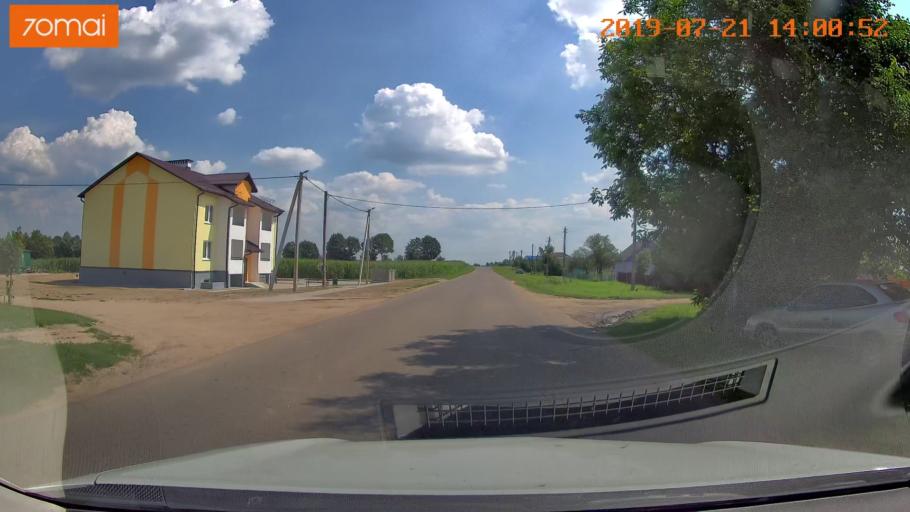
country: BY
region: Grodnenskaya
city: Lyubcha
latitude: 53.7483
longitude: 26.0688
